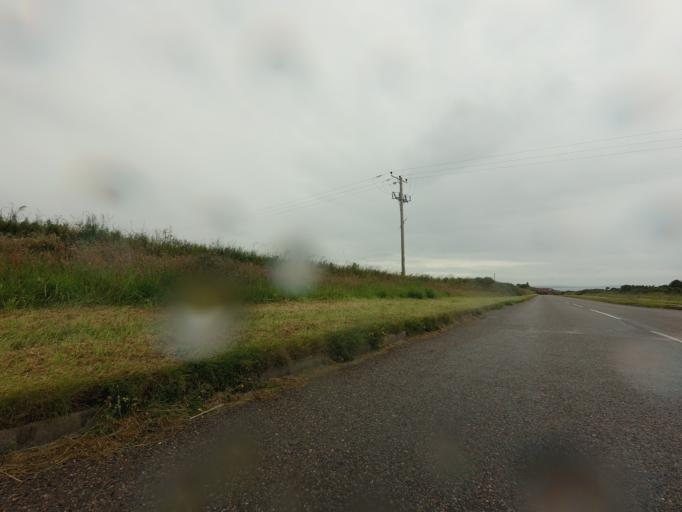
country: GB
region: Scotland
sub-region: Moray
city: Findochty
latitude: 57.6957
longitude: -2.8983
